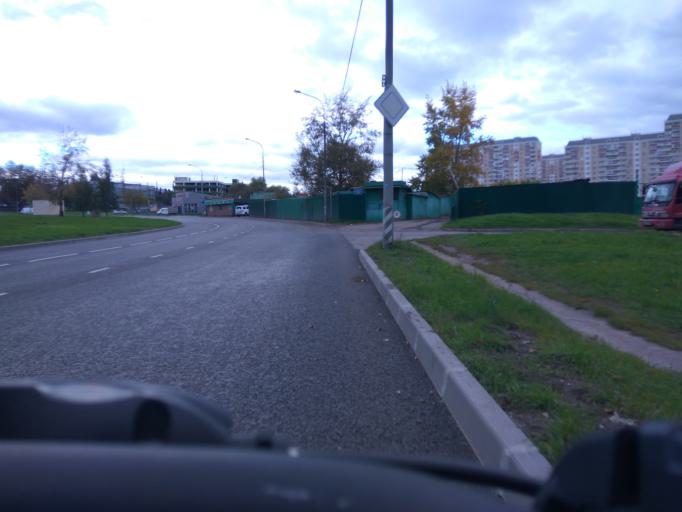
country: RU
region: Moscow
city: Kozeyevo
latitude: 55.8748
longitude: 37.6140
